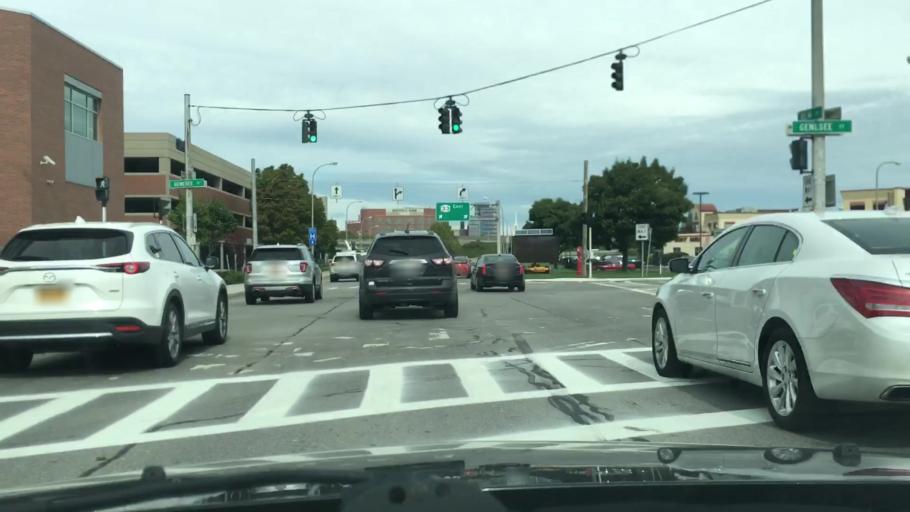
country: US
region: New York
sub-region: Erie County
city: Buffalo
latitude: 42.8905
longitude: -78.8677
